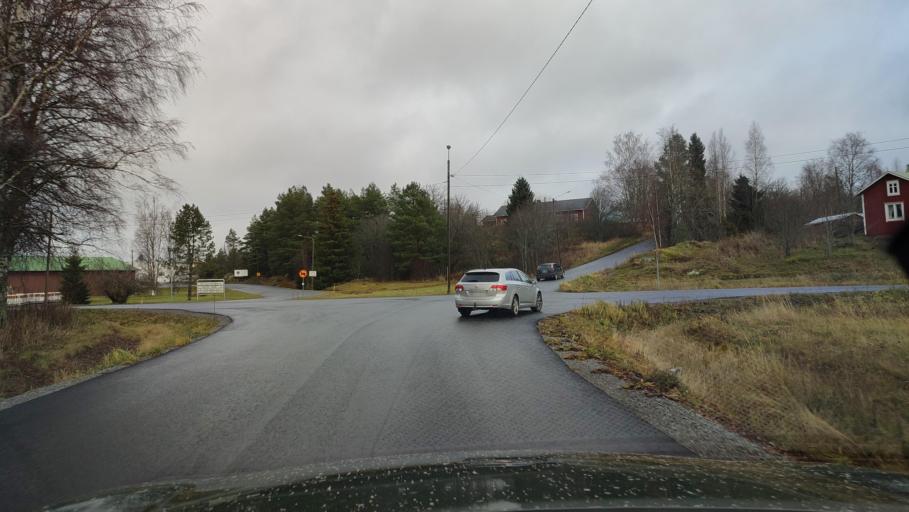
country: FI
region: Ostrobothnia
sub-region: Sydosterbotten
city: Kristinestad
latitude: 62.3002
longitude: 21.4558
